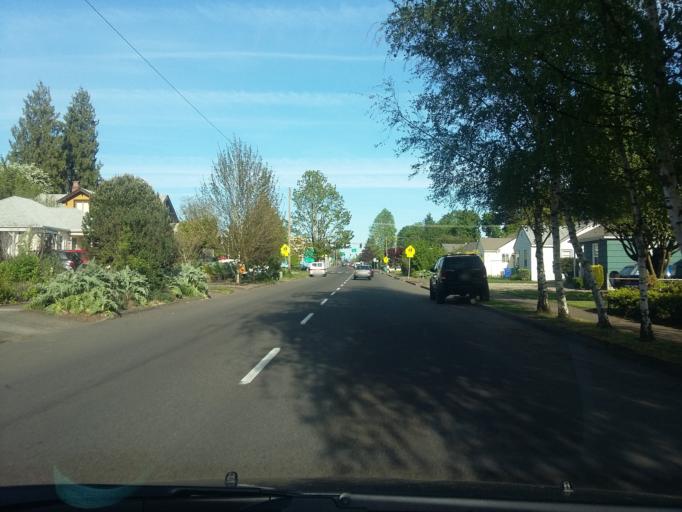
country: US
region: Oregon
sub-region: Multnomah County
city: Lents
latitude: 45.5183
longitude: -122.5709
